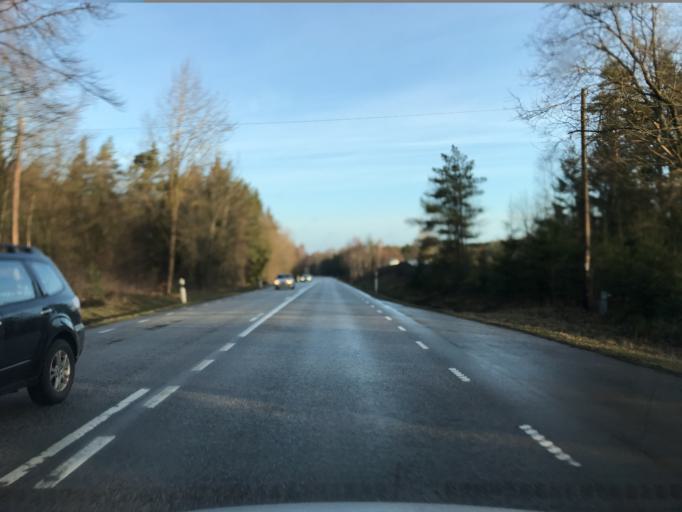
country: SE
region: Skane
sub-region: Hassleholms Kommun
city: Bjarnum
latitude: 56.2508
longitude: 13.7167
